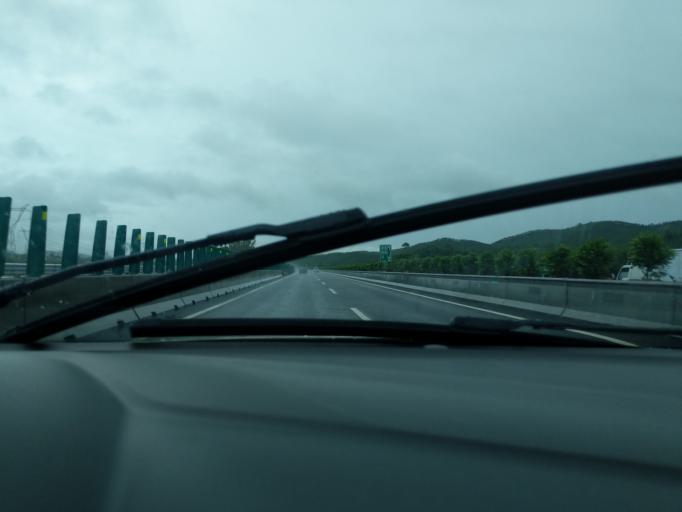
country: CN
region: Guangdong
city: Liangxi
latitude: 22.2688
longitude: 112.3252
